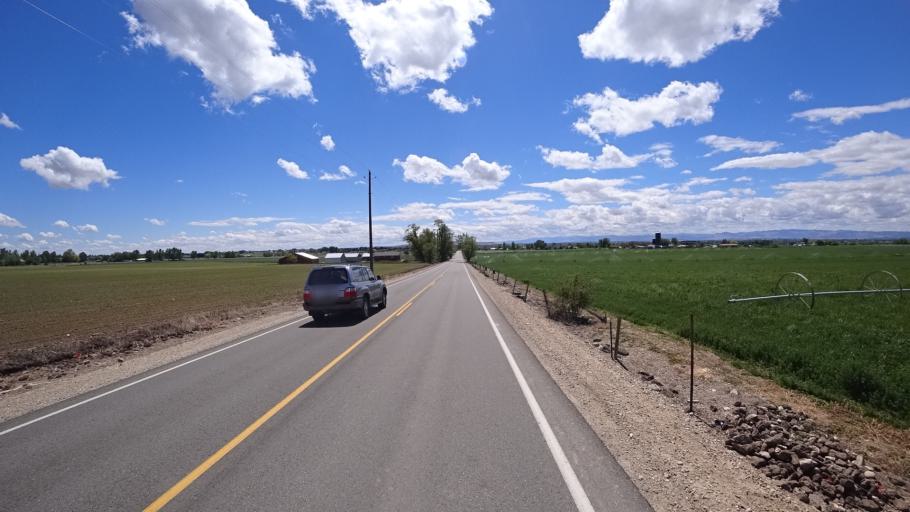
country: US
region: Idaho
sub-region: Ada County
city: Meridian
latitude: 43.5664
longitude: -116.4536
